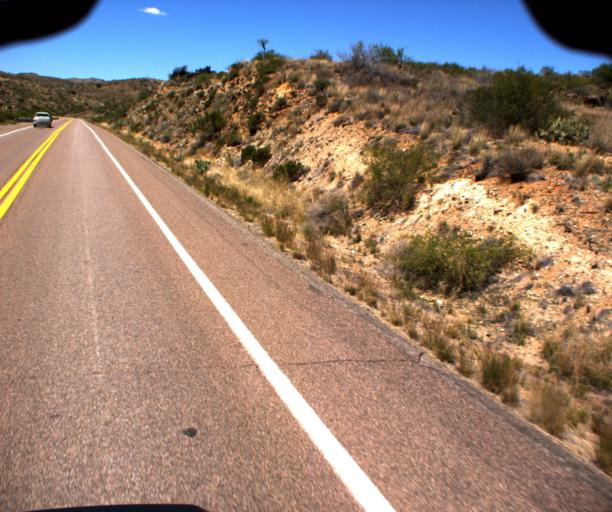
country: US
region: Arizona
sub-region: Yavapai County
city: Bagdad
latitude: 34.5437
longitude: -113.1470
